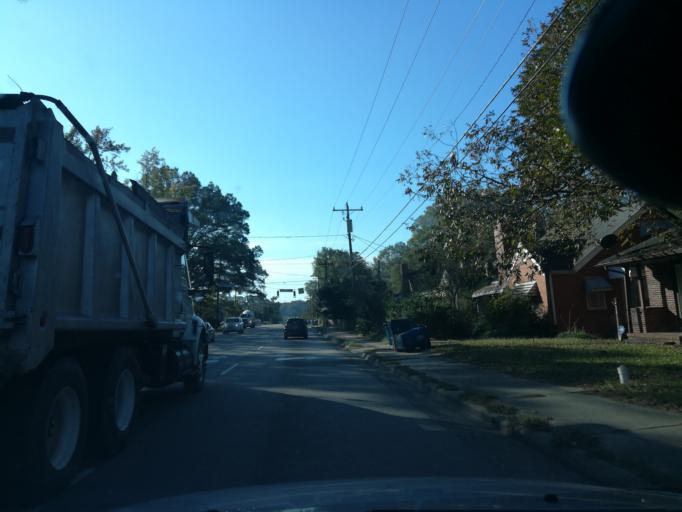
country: US
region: North Carolina
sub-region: Durham County
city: Durham
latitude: 36.0241
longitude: -78.8899
